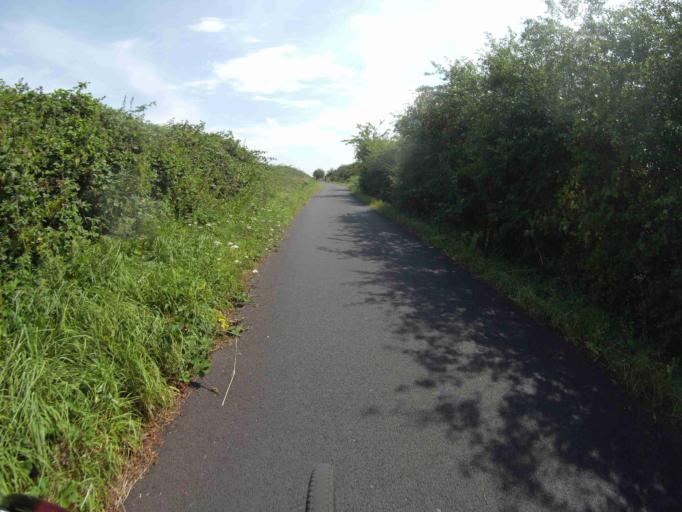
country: GB
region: England
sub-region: Devon
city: Topsham
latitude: 50.6845
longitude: -3.4786
